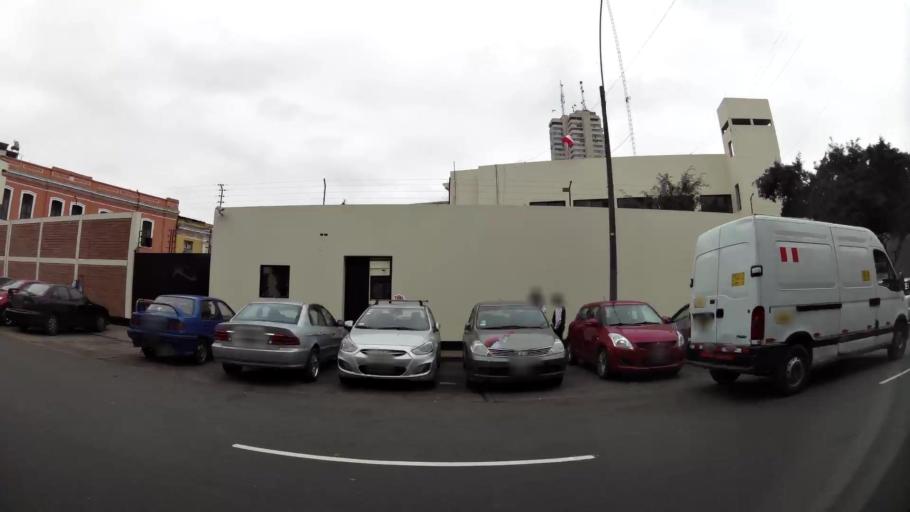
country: PE
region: Lima
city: Lima
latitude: -12.0534
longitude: -77.0368
